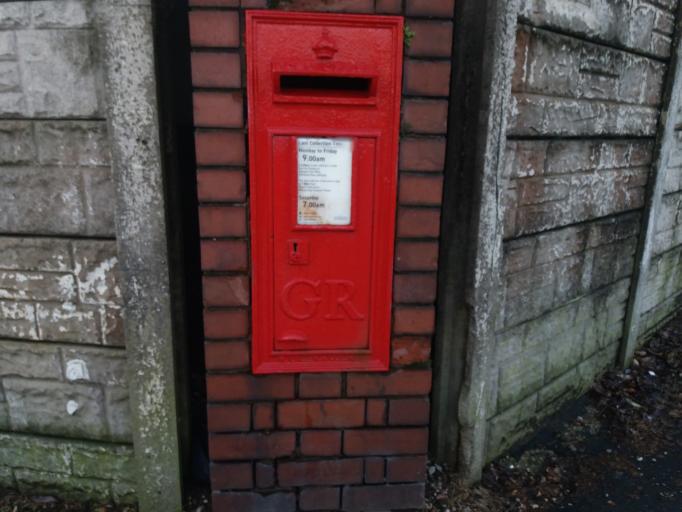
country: GB
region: England
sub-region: Lancashire
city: Adlington
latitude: 53.6094
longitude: -2.6042
